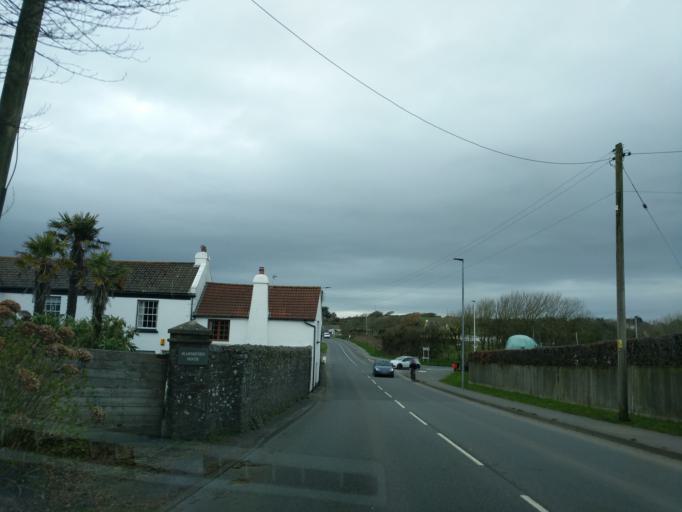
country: GB
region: England
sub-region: Devon
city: Appledore
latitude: 51.0459
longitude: -4.2023
